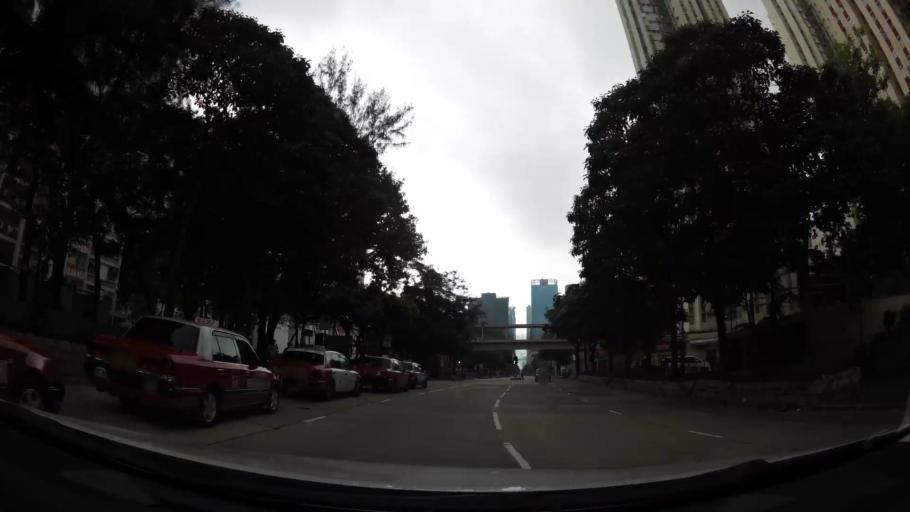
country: HK
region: Kowloon City
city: Kowloon
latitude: 22.3297
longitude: 114.2082
